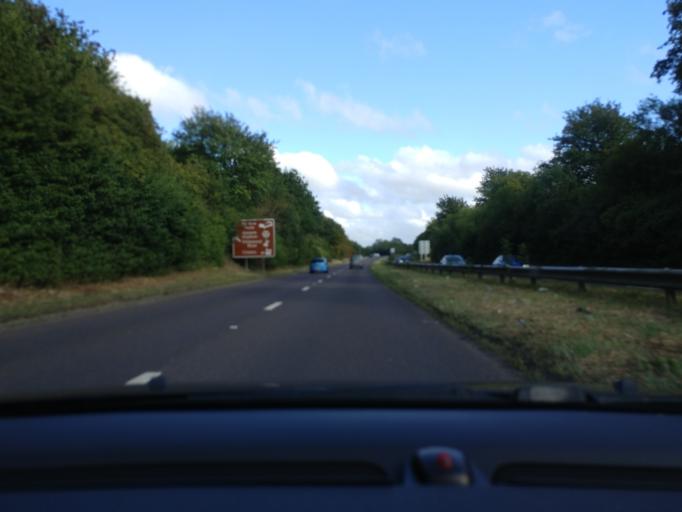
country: GB
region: England
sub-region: Oxfordshire
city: Cowley
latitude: 51.7158
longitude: -1.2281
